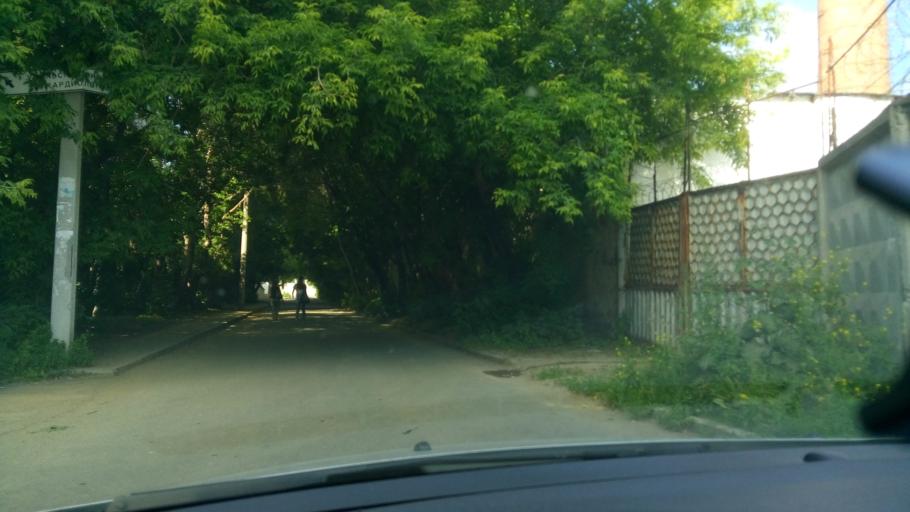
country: RU
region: Sverdlovsk
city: Yekaterinburg
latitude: 56.8200
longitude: 60.6002
